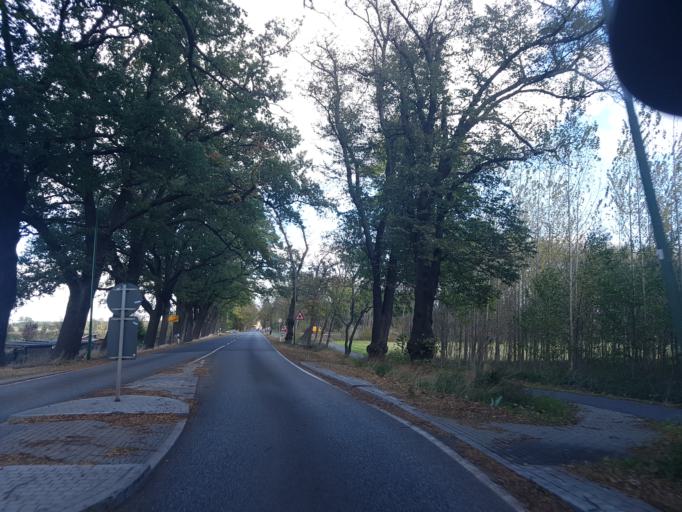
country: DE
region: Brandenburg
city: Nauen
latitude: 52.6177
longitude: 12.8891
